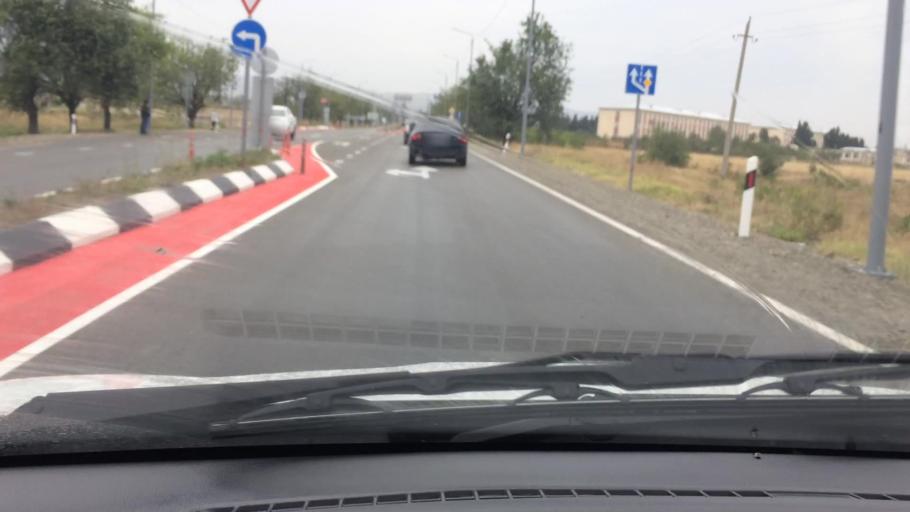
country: GE
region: Kvemo Kartli
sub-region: Marneuli
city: Marneuli
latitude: 41.5704
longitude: 44.7751
